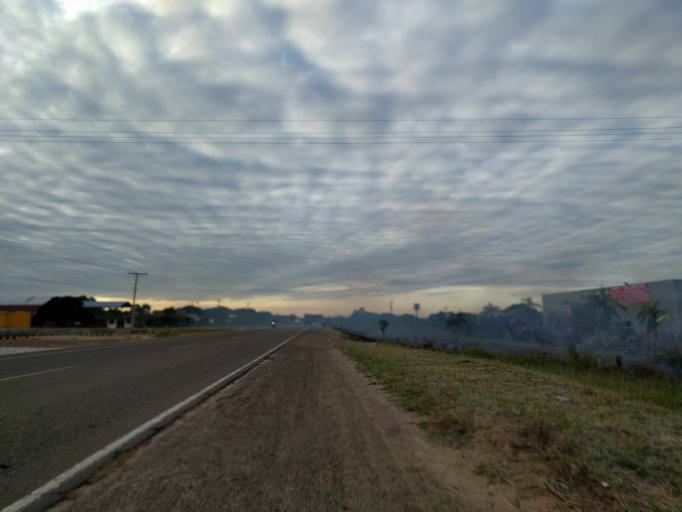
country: BO
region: Santa Cruz
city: Santa Rita
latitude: -17.8839
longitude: -63.2655
